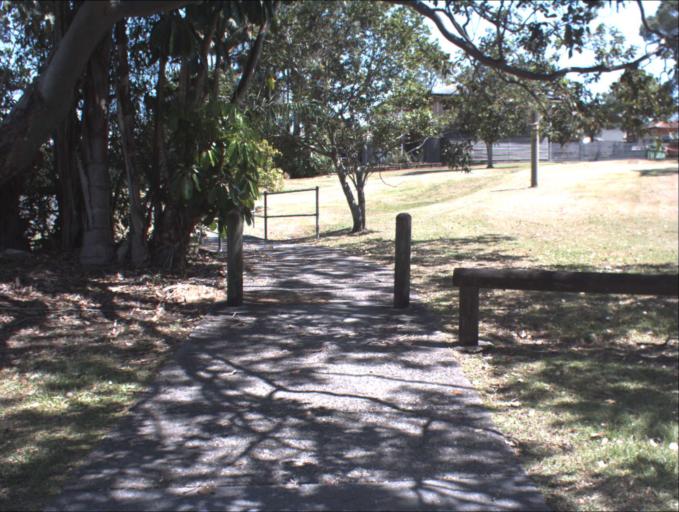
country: AU
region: Queensland
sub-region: Logan
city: Rochedale South
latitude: -27.5913
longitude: 153.1422
